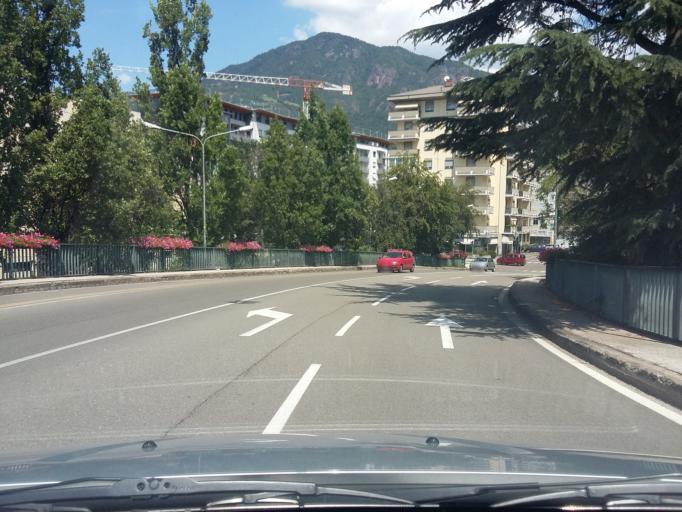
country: IT
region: Trentino-Alto Adige
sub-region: Bolzano
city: Bolzano
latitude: 46.4873
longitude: 11.3310
